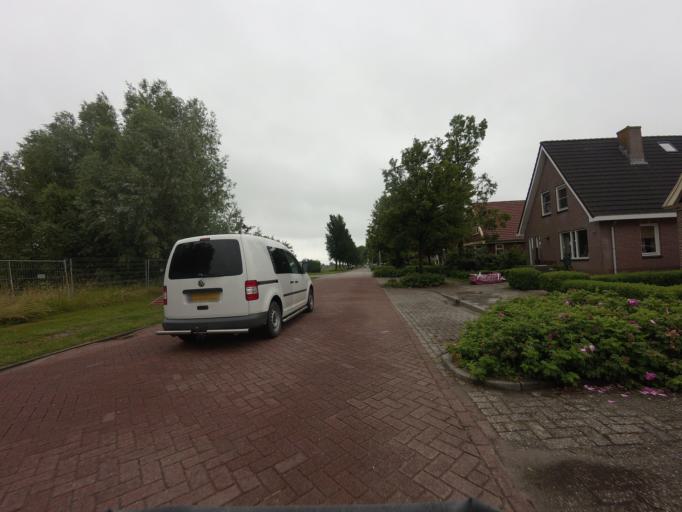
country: NL
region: North Holland
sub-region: Gemeente Schagen
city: Schagen
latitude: 52.7701
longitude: 4.8821
